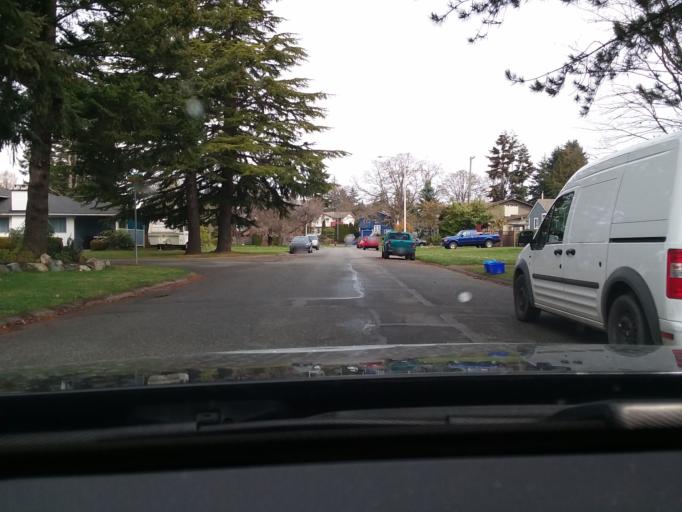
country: CA
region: British Columbia
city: Oak Bay
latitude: 48.4740
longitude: -123.3301
